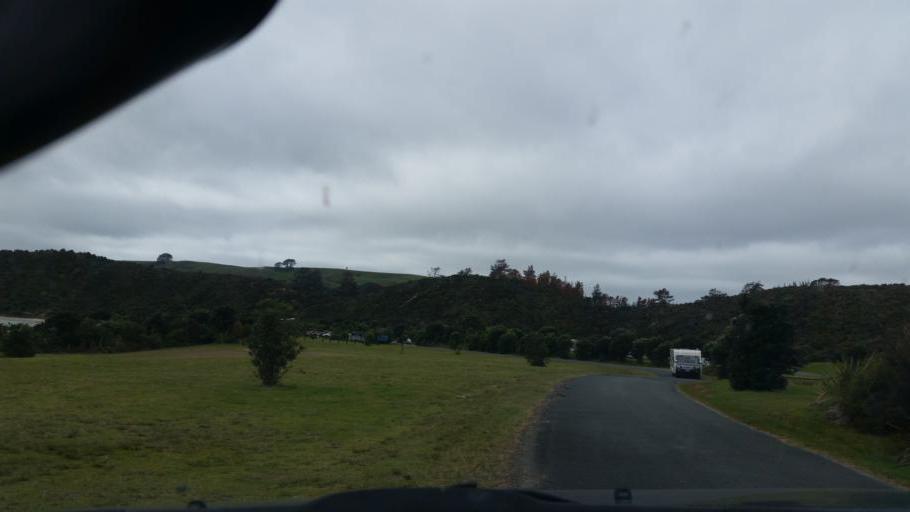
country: NZ
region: Northland
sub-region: Kaipara District
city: Dargaville
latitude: -35.8109
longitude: 173.6618
